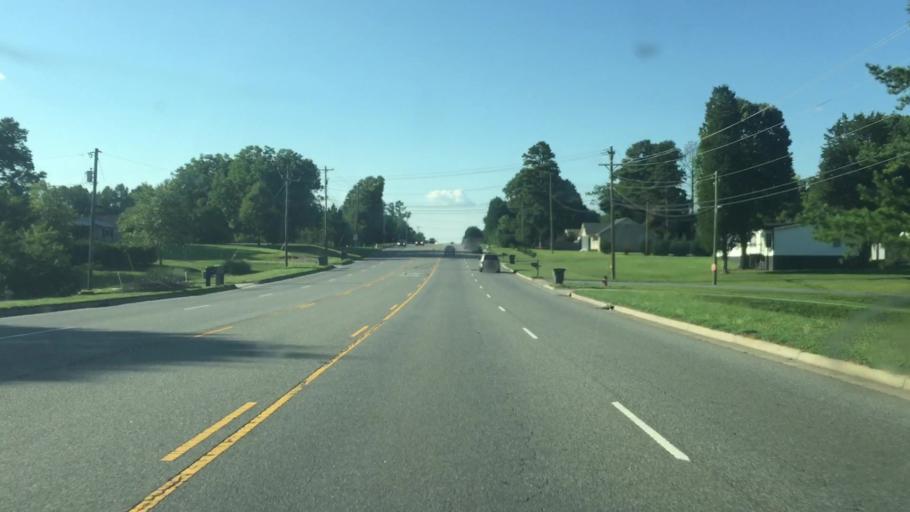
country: US
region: North Carolina
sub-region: Cabarrus County
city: Kannapolis
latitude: 35.4265
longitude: -80.6788
